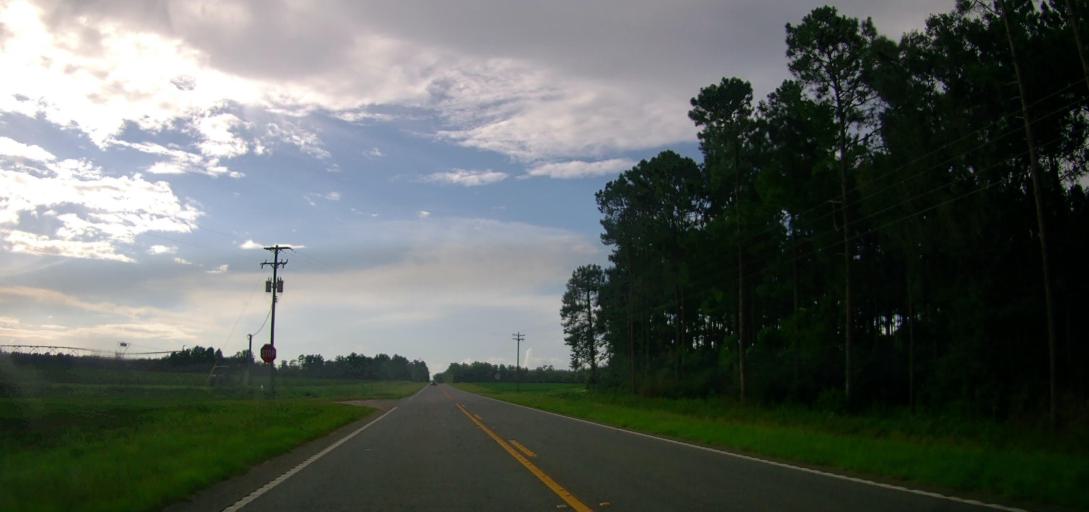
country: US
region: Georgia
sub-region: Ware County
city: Deenwood
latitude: 31.3157
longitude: -82.5714
